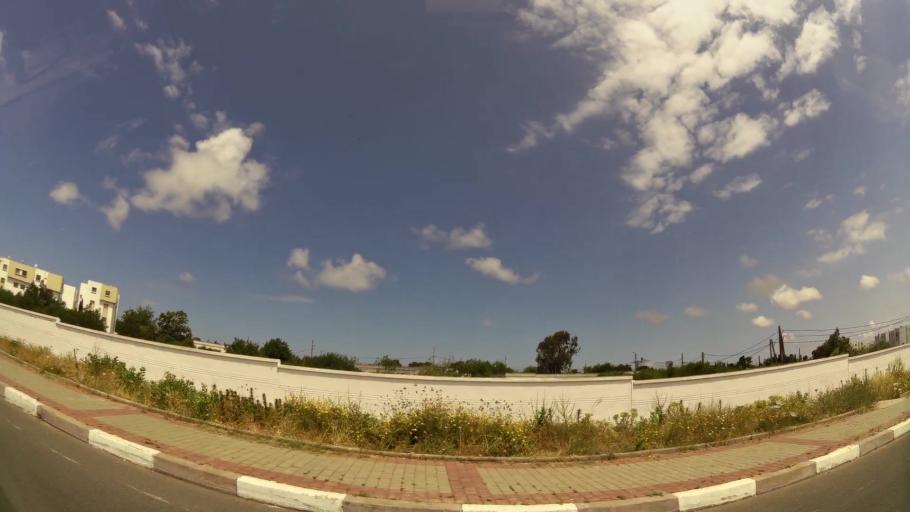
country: MA
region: Gharb-Chrarda-Beni Hssen
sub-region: Kenitra Province
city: Kenitra
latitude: 34.2767
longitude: -6.6095
